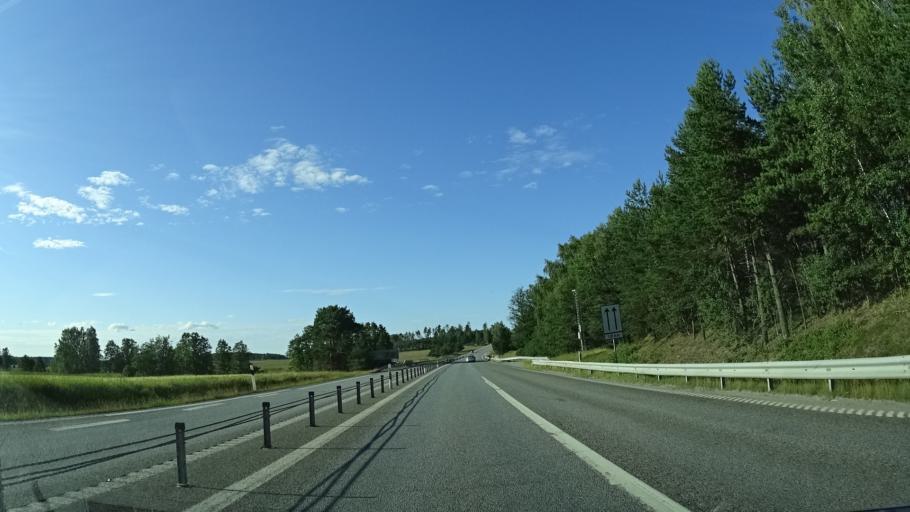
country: SE
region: Stockholm
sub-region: Osterakers Kommun
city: Akersberga
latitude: 59.5626
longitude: 18.2316
